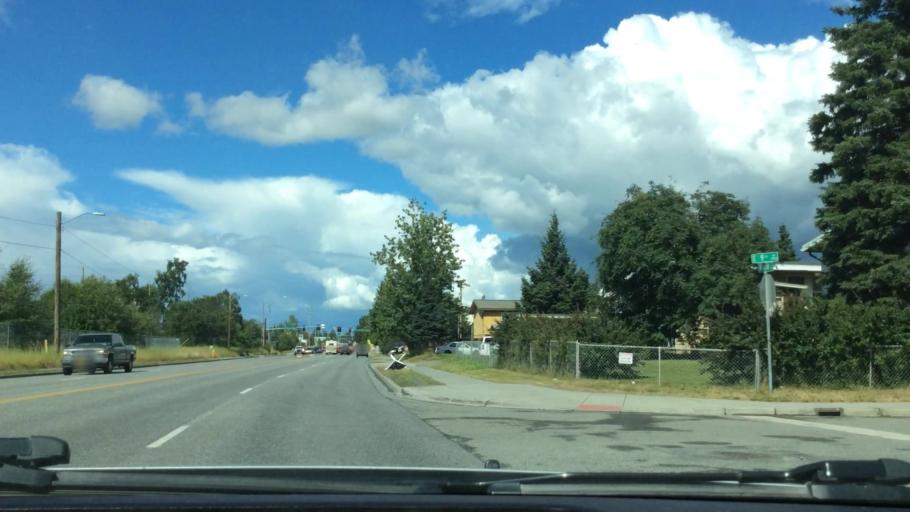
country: US
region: Alaska
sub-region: Anchorage Municipality
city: Anchorage
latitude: 61.2138
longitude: -149.8082
